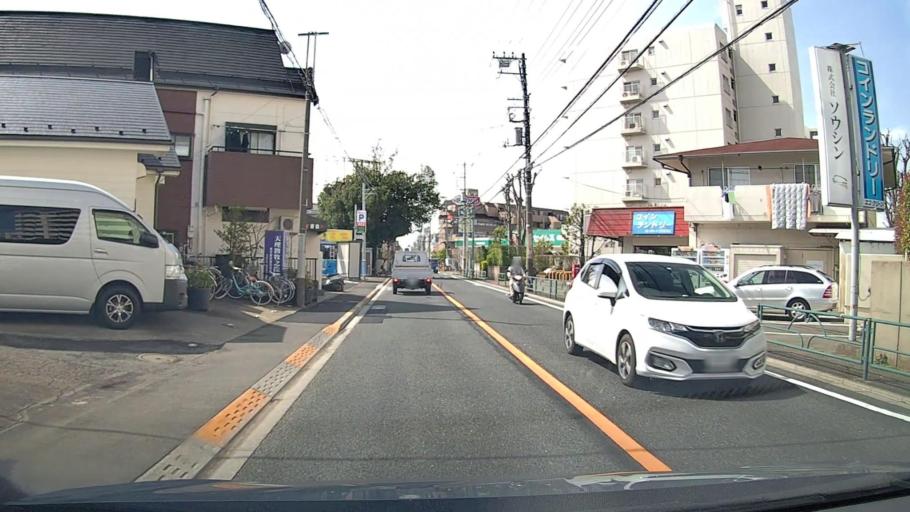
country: JP
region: Tokyo
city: Nishi-Tokyo-shi
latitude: 35.7341
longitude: 139.5504
